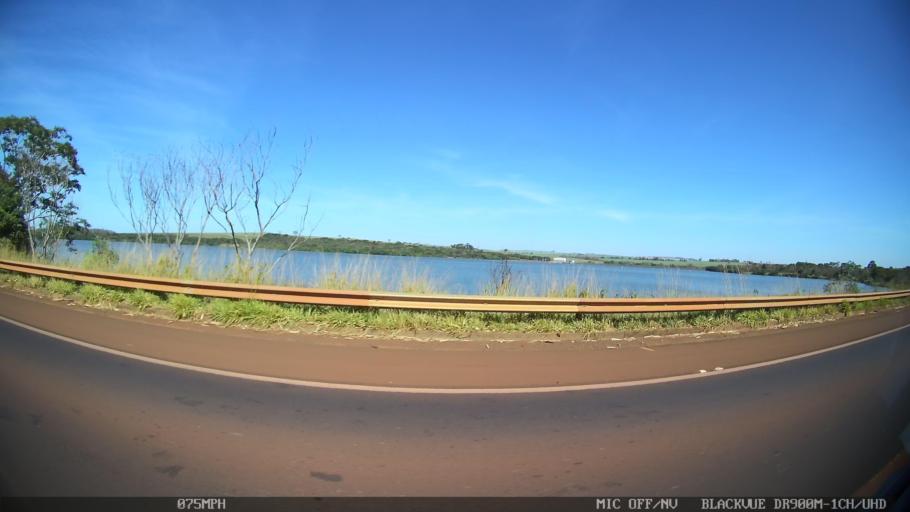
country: BR
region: Sao Paulo
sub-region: Sao Joaquim Da Barra
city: Sao Joaquim da Barra
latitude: -20.5406
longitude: -47.8097
